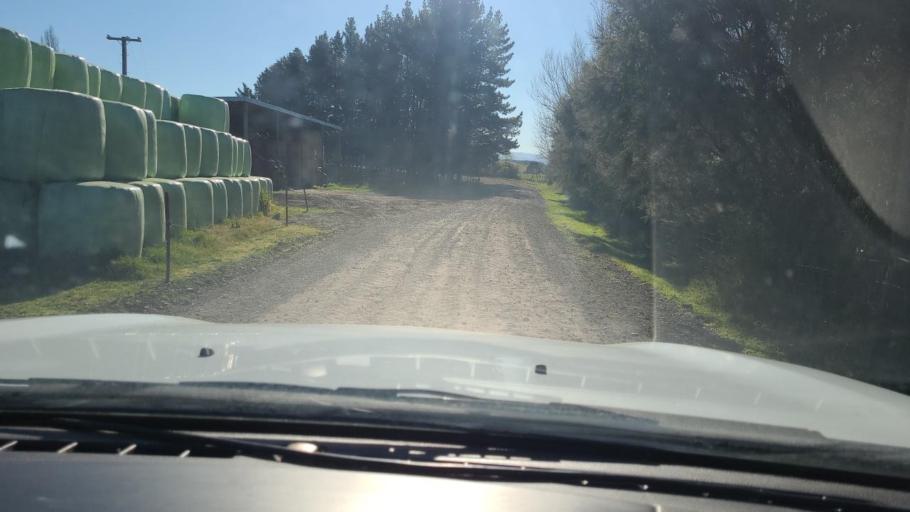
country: NZ
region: Hawke's Bay
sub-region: Napier City
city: Taradale
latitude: -39.4592
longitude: 176.6324
